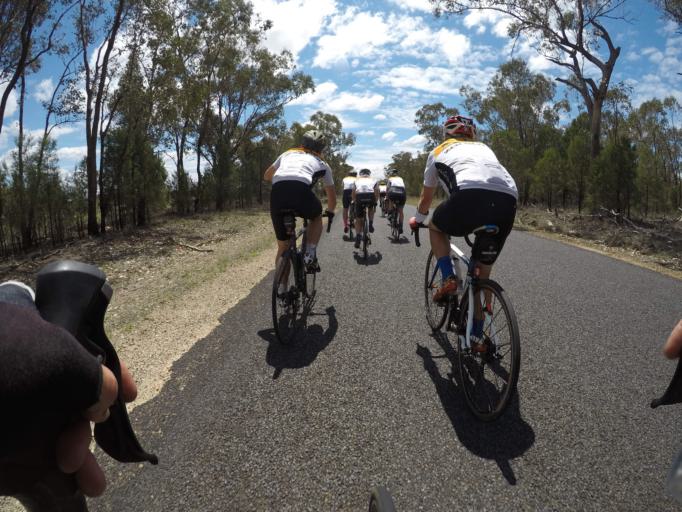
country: AU
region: New South Wales
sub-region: Dubbo Municipality
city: Dubbo
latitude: -32.3707
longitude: 148.5811
